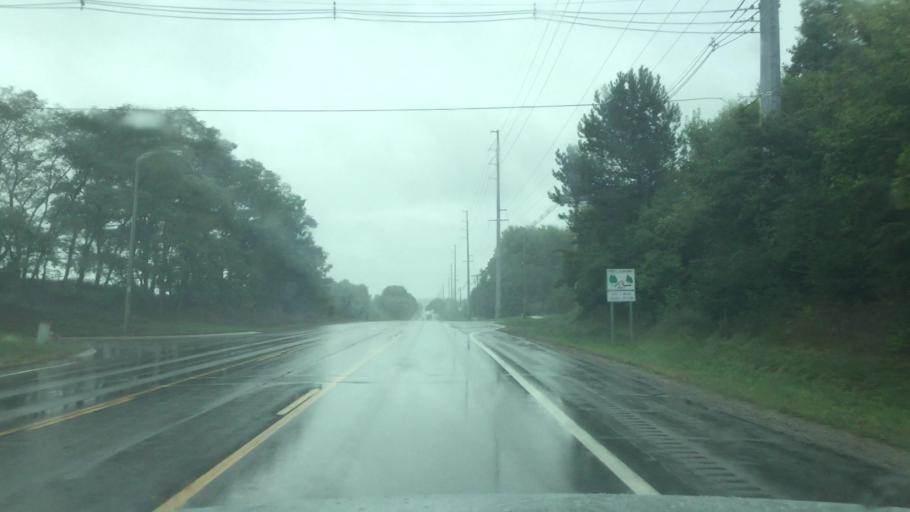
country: US
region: Michigan
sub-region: Livingston County
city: Brighton
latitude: 42.6320
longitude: -83.7778
